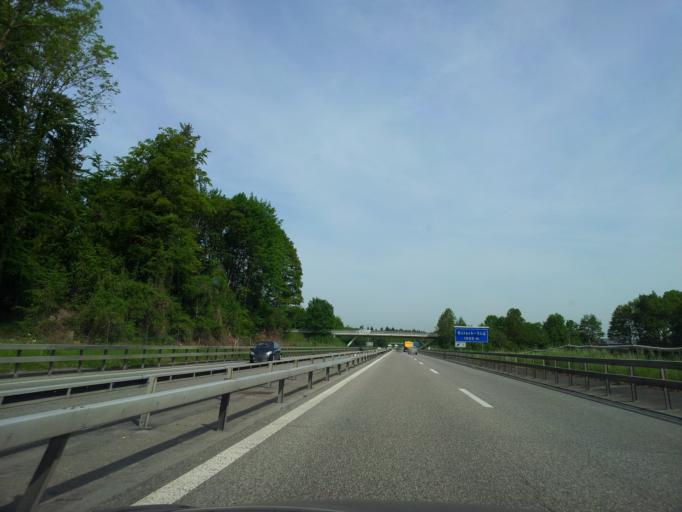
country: CH
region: Zurich
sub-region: Bezirk Buelach
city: Bachenbulach
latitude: 47.4936
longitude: 8.5394
